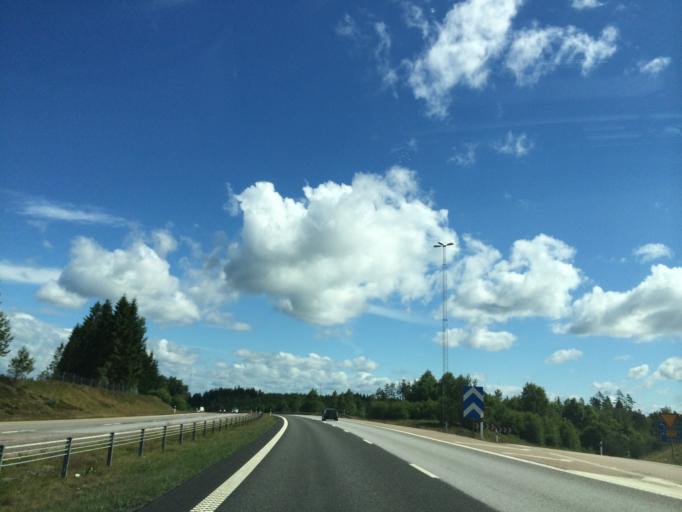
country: SE
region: Kronoberg
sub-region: Markaryds Kommun
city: Stromsnasbruk
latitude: 56.6209
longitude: 13.7809
